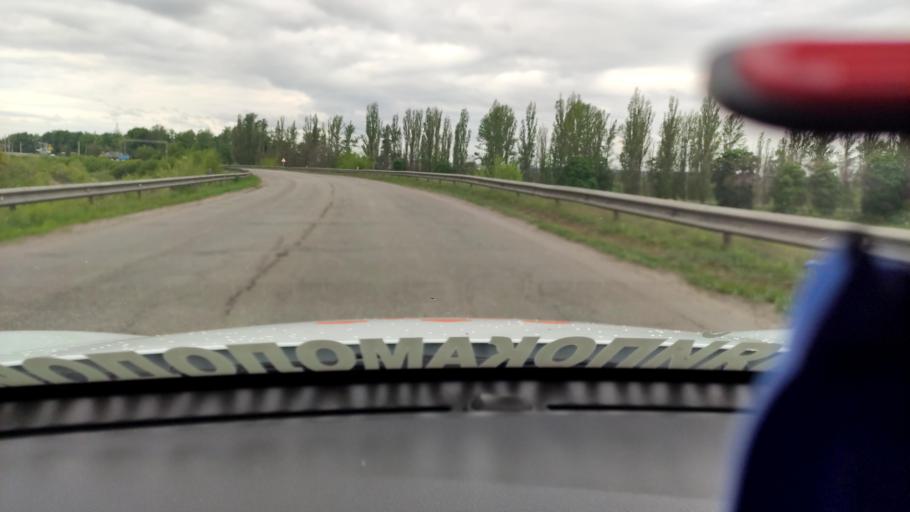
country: RU
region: Voronezj
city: Liski
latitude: 51.0119
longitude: 39.5553
